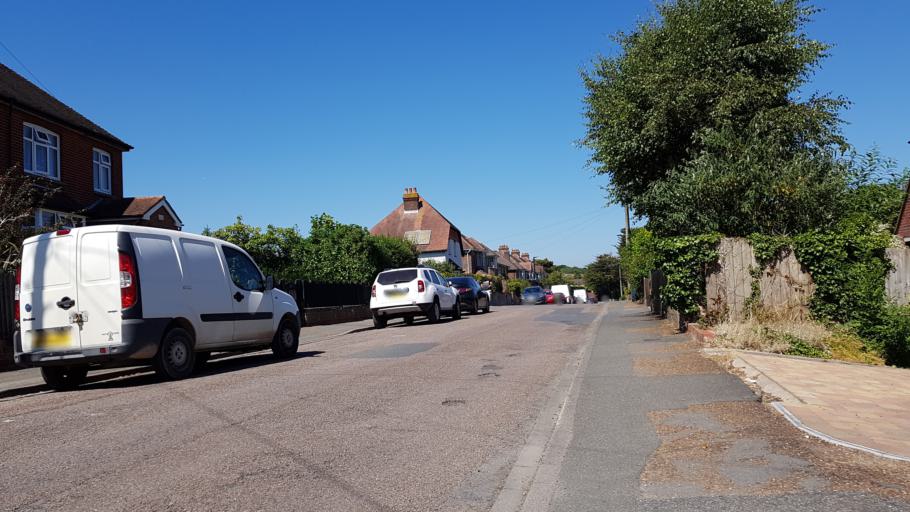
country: GB
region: England
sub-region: Isle of Wight
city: Newport
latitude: 50.6963
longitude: -1.3049
